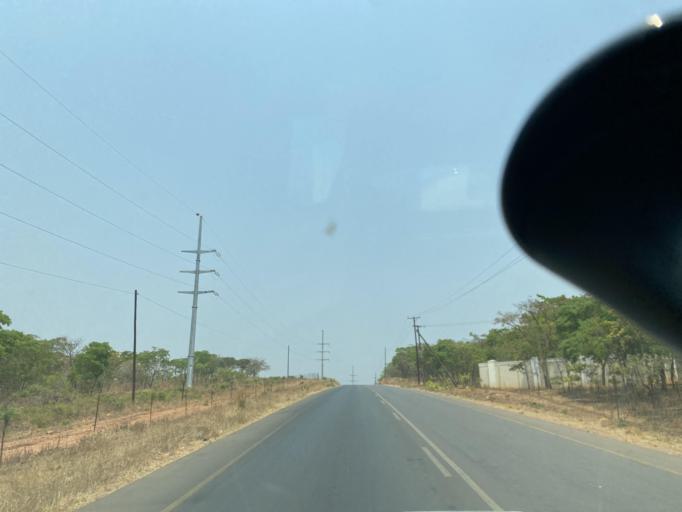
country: ZM
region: Lusaka
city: Lusaka
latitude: -15.5310
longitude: 28.4669
